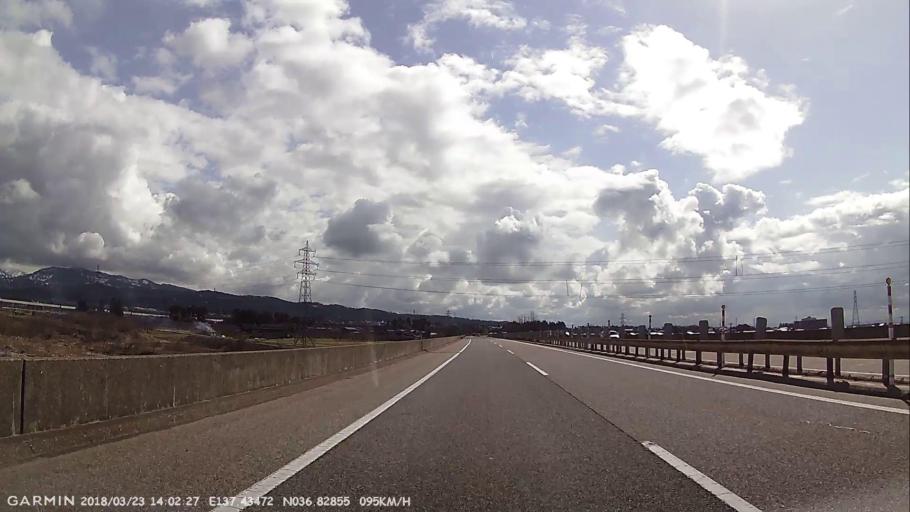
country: JP
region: Toyama
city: Uozu
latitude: 36.8283
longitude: 137.4346
